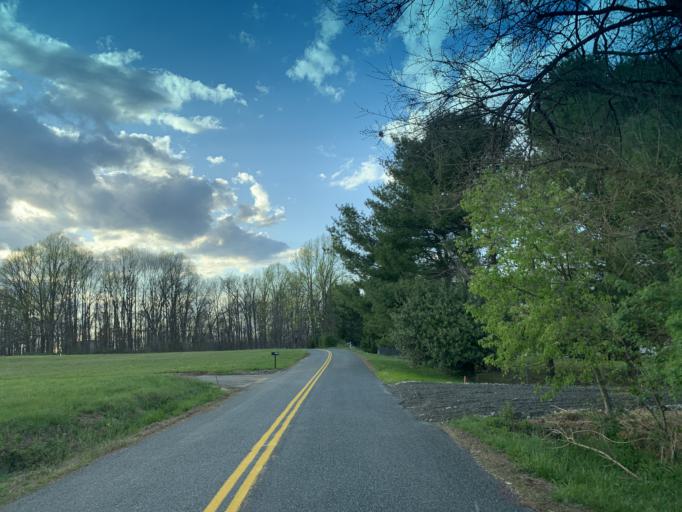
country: US
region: Maryland
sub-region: Harford County
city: South Bel Air
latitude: 39.6131
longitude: -76.2996
